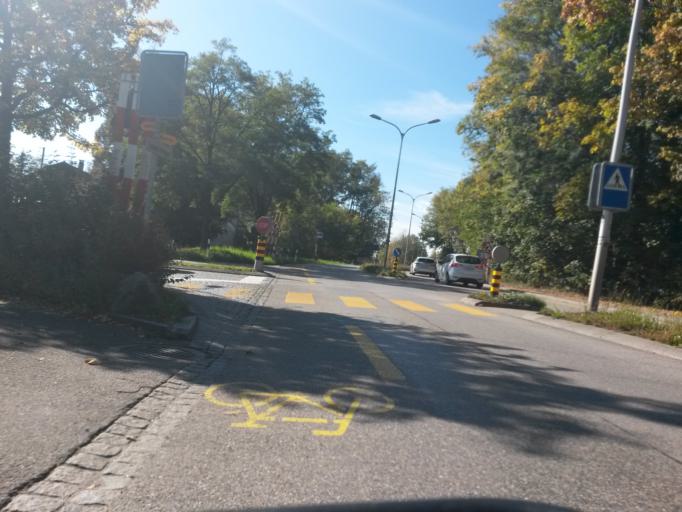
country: CH
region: Solothurn
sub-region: Bezirk Wasseramt
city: Luterbach
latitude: 47.2149
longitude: 7.5757
